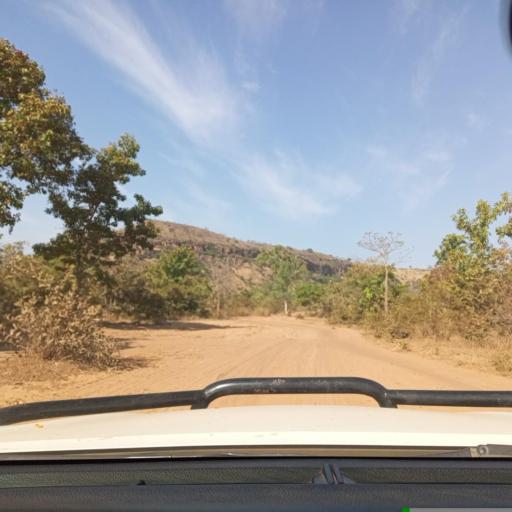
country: ML
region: Bamako
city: Bamako
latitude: 12.5567
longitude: -8.1479
